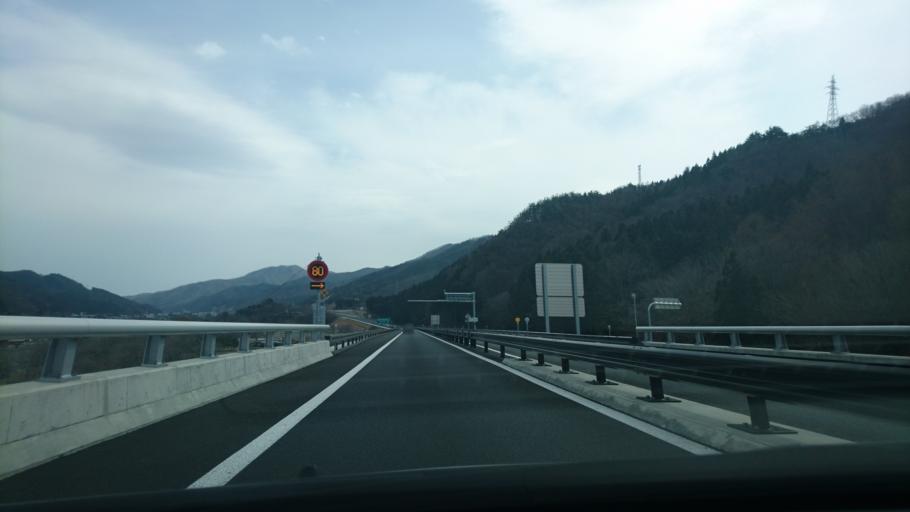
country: JP
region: Iwate
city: Kamaishi
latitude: 39.2524
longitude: 141.7782
